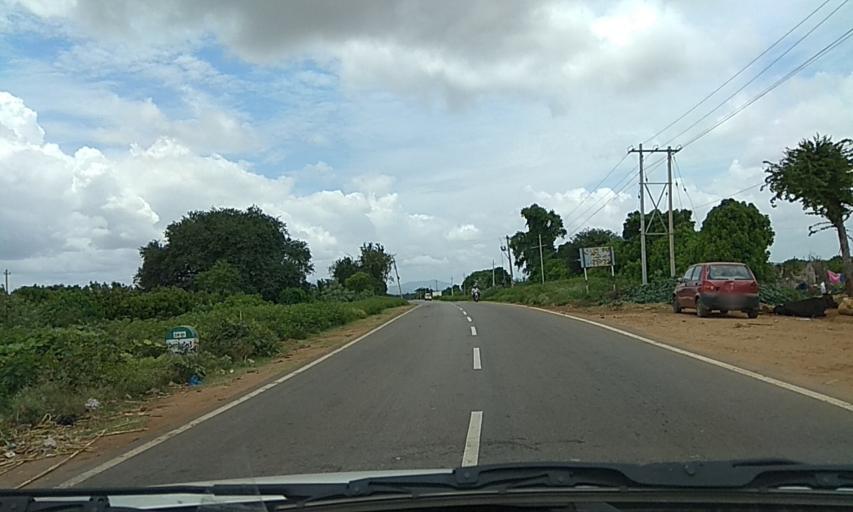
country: IN
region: Karnataka
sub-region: Chamrajnagar
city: Gundlupet
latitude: 11.8153
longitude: 76.7542
